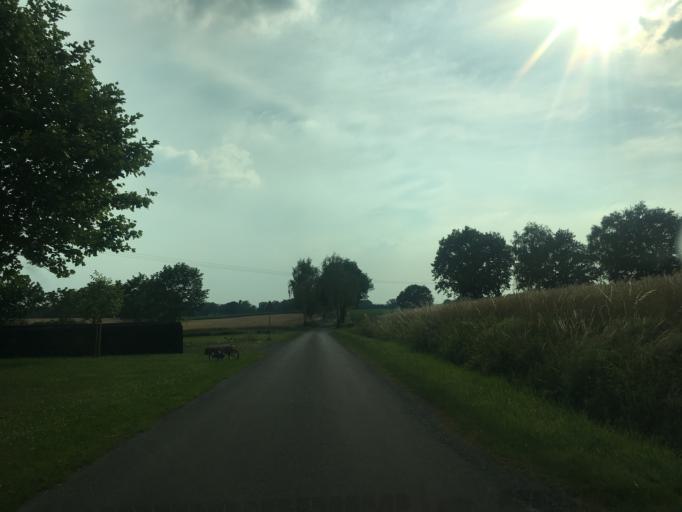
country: DE
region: North Rhine-Westphalia
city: Olfen
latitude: 51.7465
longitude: 7.3581
